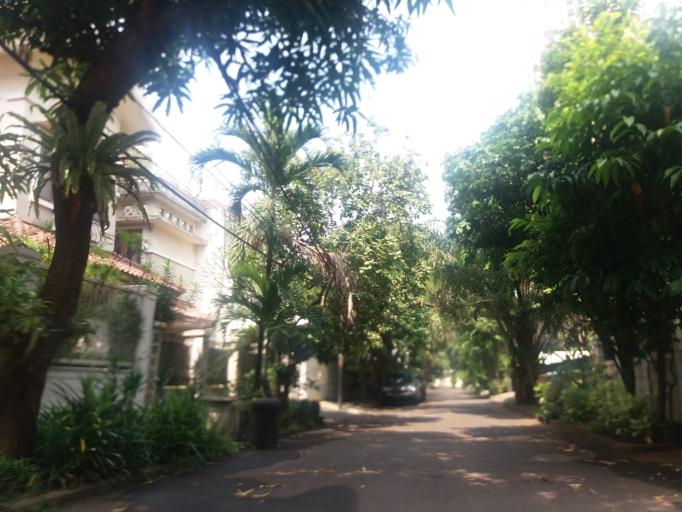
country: ID
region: Jakarta Raya
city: Jakarta
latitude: -6.2268
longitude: 106.8283
